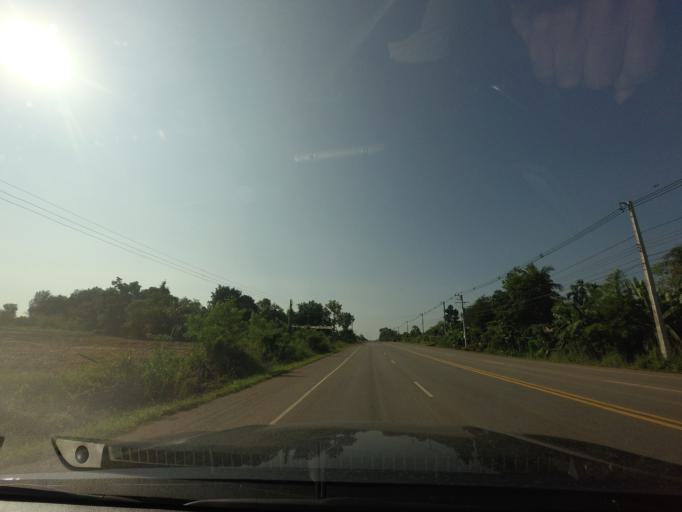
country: TH
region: Phetchabun
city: Lom Kao
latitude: 16.8270
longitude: 101.1810
